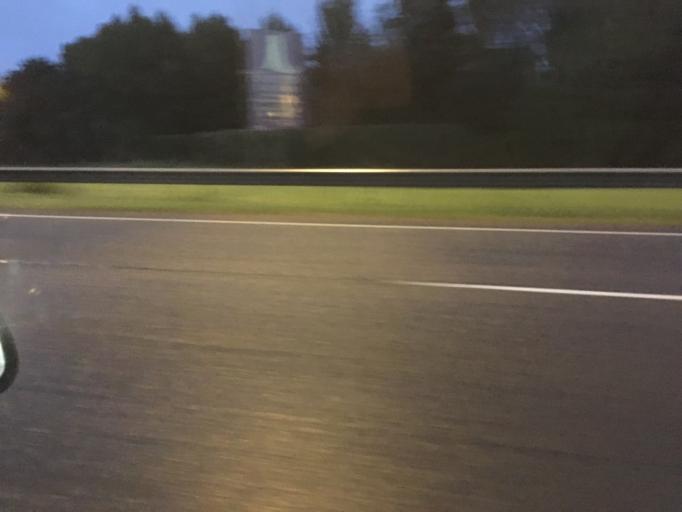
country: IE
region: Leinster
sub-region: South Dublin
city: Saggart
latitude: 53.2918
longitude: -6.4386
